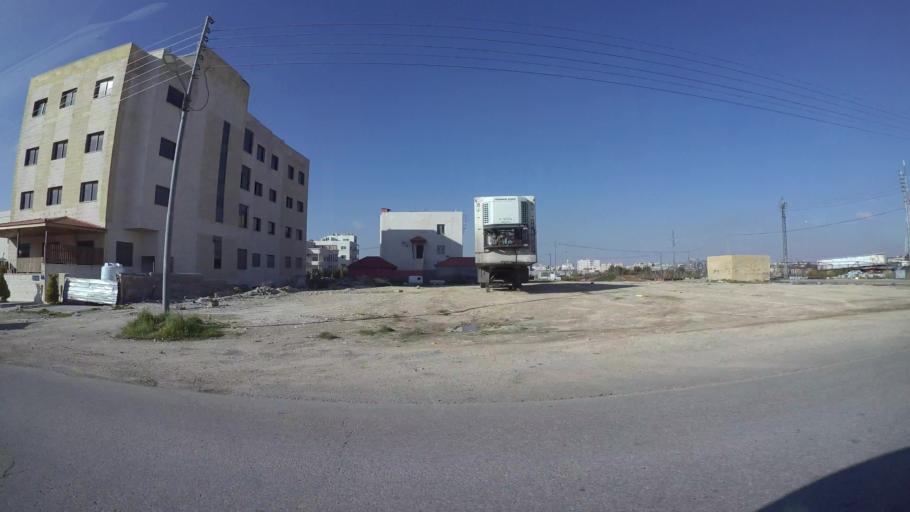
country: JO
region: Amman
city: Al Quwaysimah
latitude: 31.9024
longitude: 35.9245
